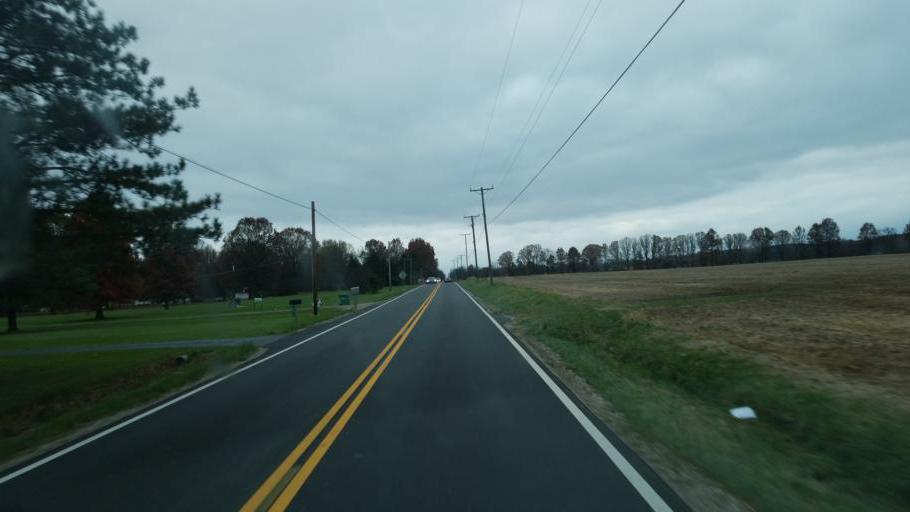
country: US
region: Ohio
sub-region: Delaware County
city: Sunbury
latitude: 40.2845
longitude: -82.9075
